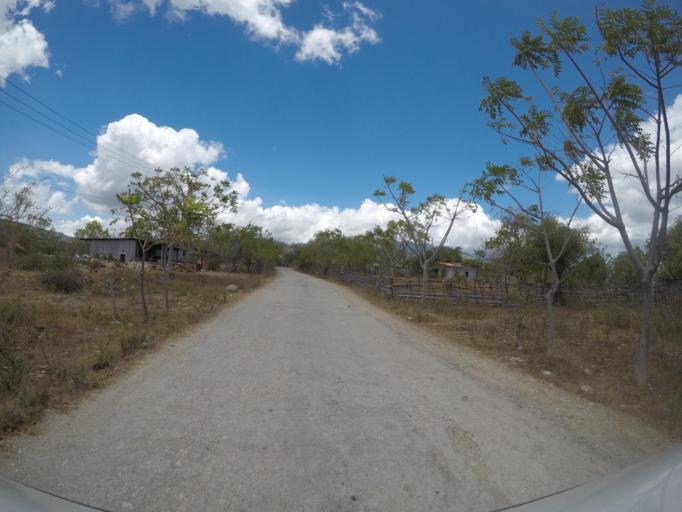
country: TL
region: Baucau
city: Baucau
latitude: -8.4834
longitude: 126.6136
